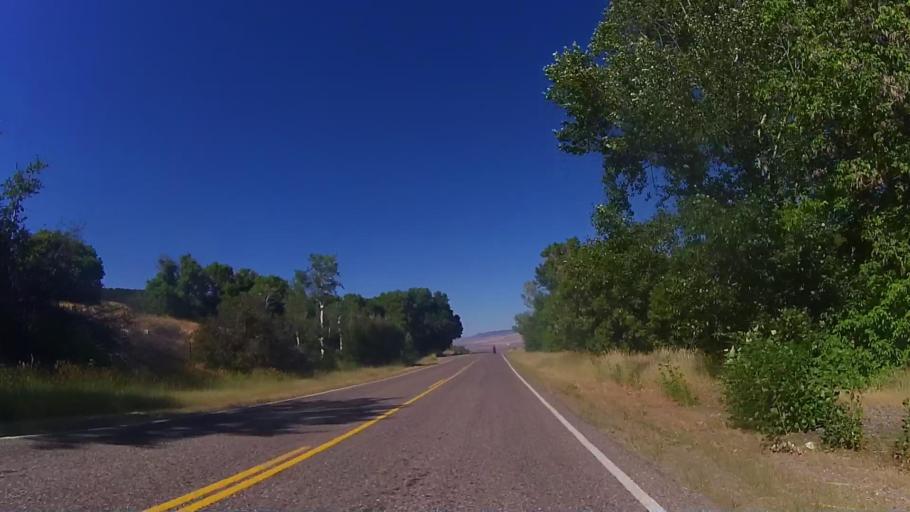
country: US
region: Idaho
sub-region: Oneida County
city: Malad City
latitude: 42.3512
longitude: -112.2237
